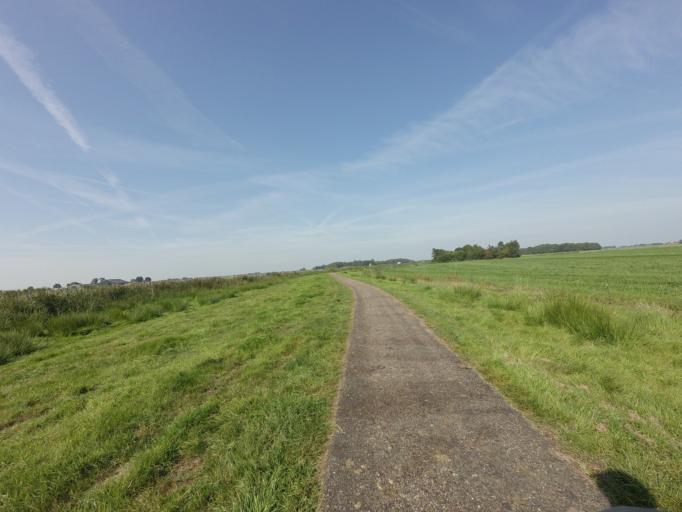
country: NL
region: Overijssel
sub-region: Gemeente Steenwijkerland
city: Oldemarkt
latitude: 52.8351
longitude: 5.9538
